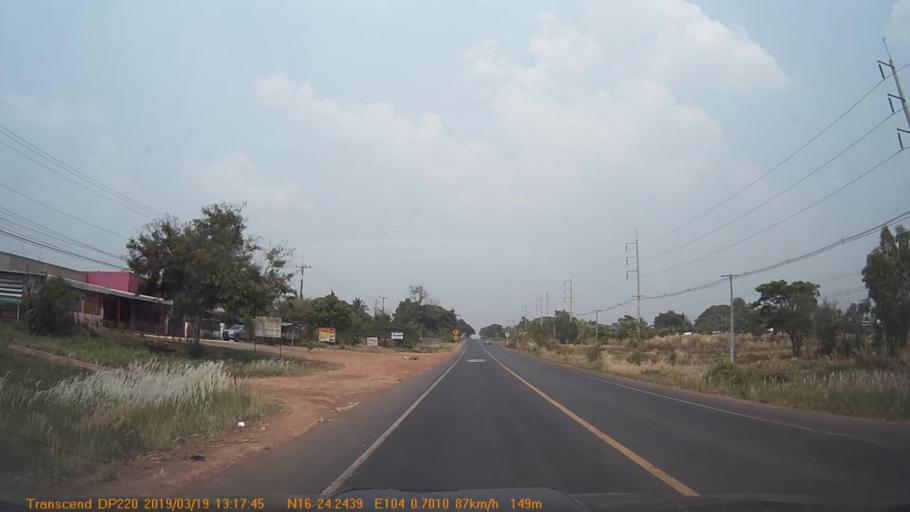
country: TH
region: Roi Et
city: Waeng
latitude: 16.4046
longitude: 104.0119
